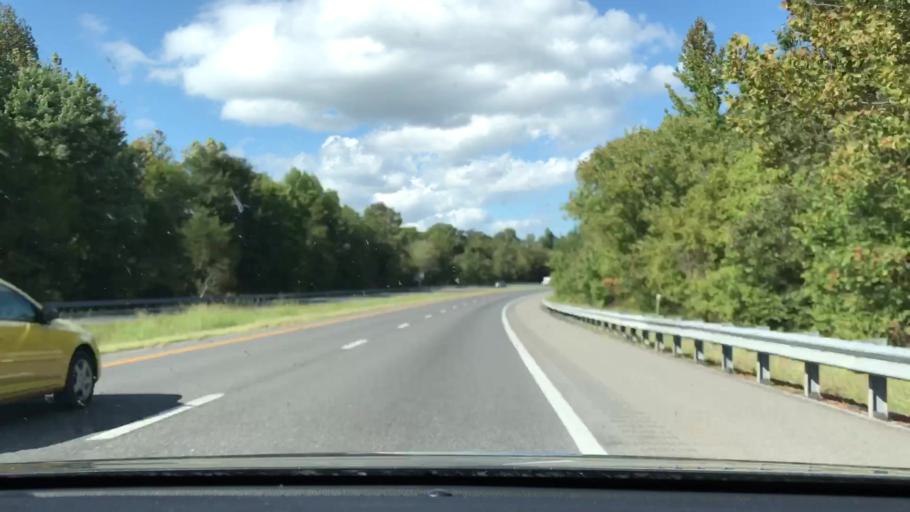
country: US
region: Kentucky
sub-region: Marshall County
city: Benton
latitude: 36.9179
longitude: -88.3511
